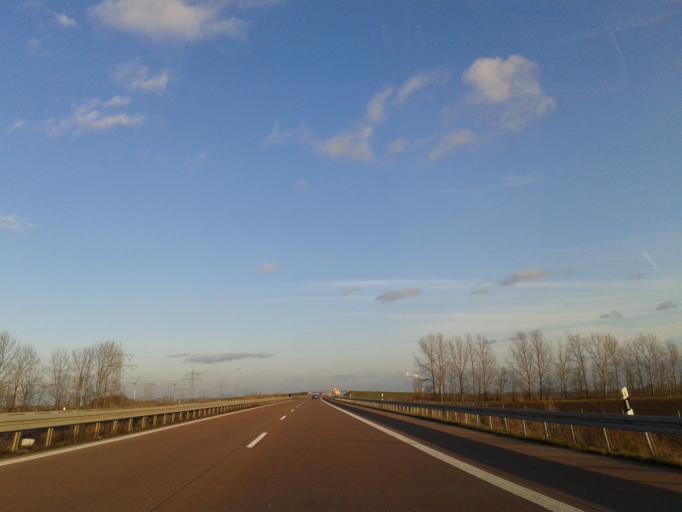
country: DE
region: Saxony-Anhalt
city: Schafstadt
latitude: 51.4043
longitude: 11.8097
